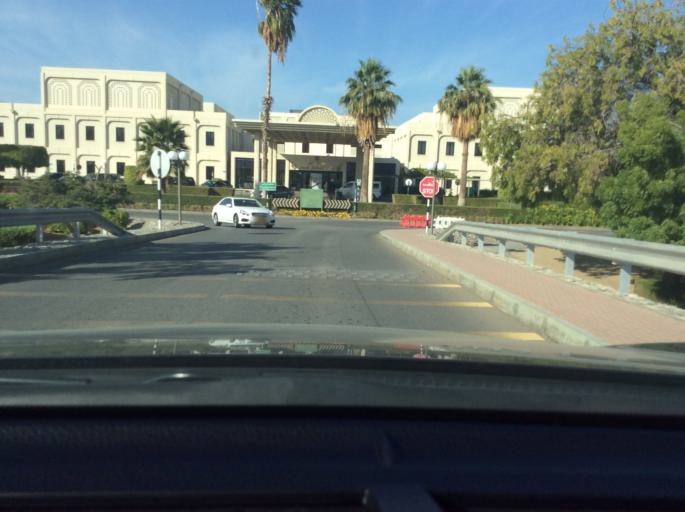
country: OM
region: Muhafazat Masqat
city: As Sib al Jadidah
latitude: 23.5869
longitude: 58.1707
